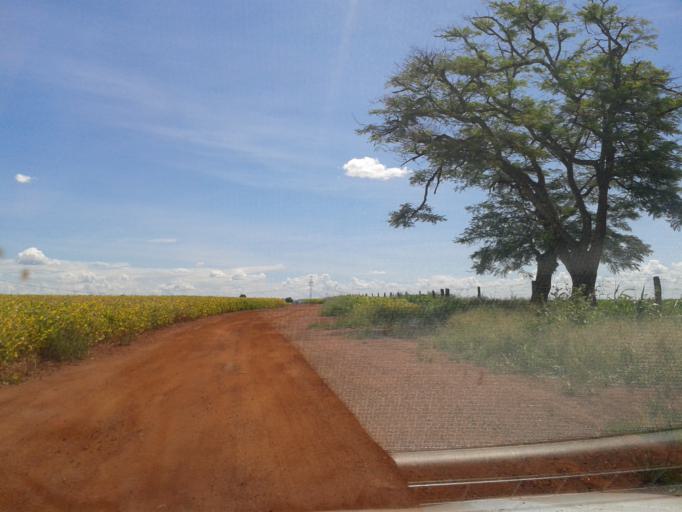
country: BR
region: Minas Gerais
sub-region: Capinopolis
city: Capinopolis
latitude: -18.7036
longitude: -49.7743
